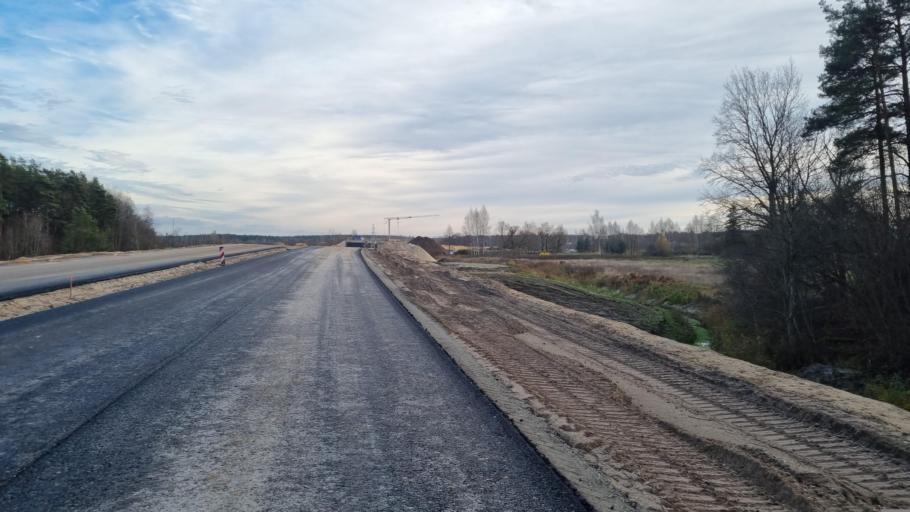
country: LV
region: Kekava
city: Kekava
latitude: 56.8197
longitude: 24.1797
